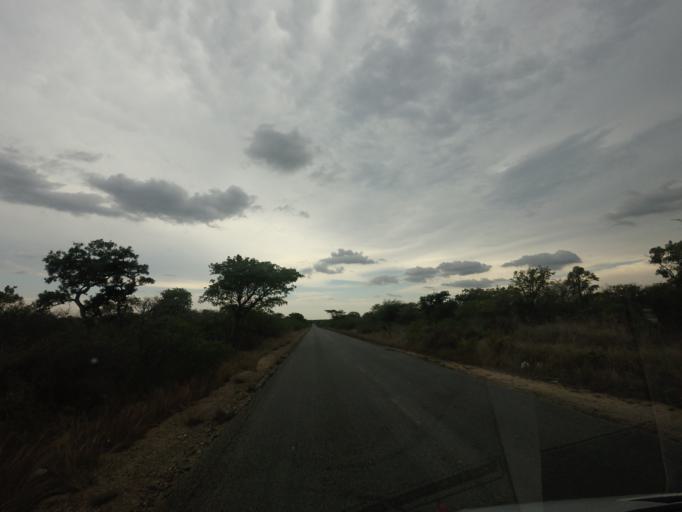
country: ZA
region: Limpopo
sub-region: Mopani District Municipality
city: Hoedspruit
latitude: -24.5287
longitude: 30.9799
